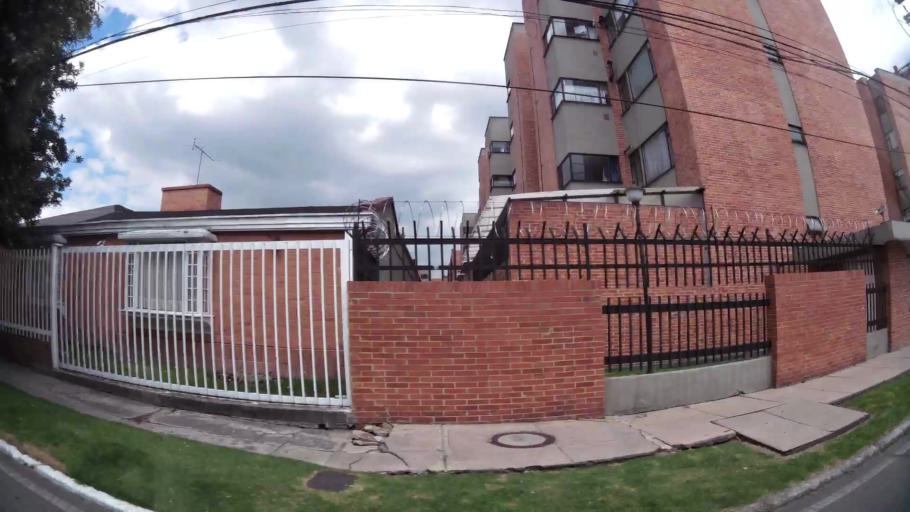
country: CO
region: Bogota D.C.
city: Barrio San Luis
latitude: 4.7067
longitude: -74.0630
